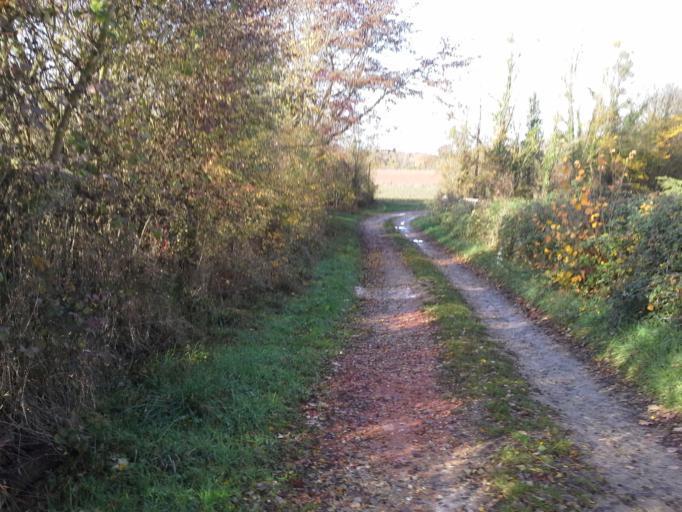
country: FR
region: Poitou-Charentes
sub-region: Departement de la Vienne
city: Pleumartin
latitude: 46.6384
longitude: 0.7541
